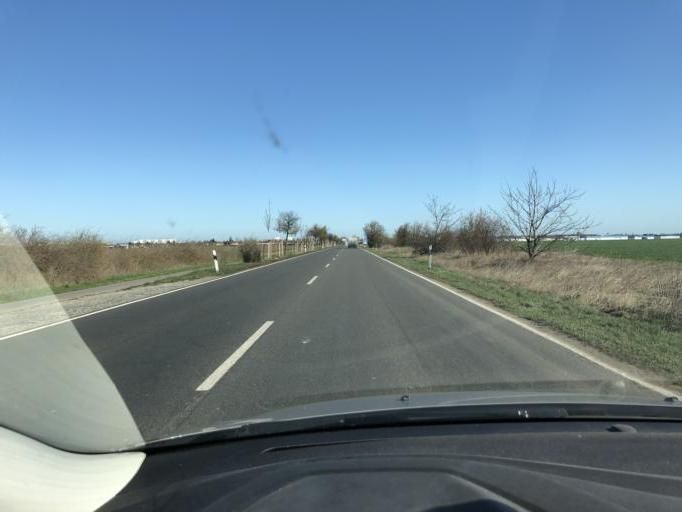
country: DE
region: Saxony-Anhalt
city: Magdeburg
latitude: 52.0694
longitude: 11.6161
